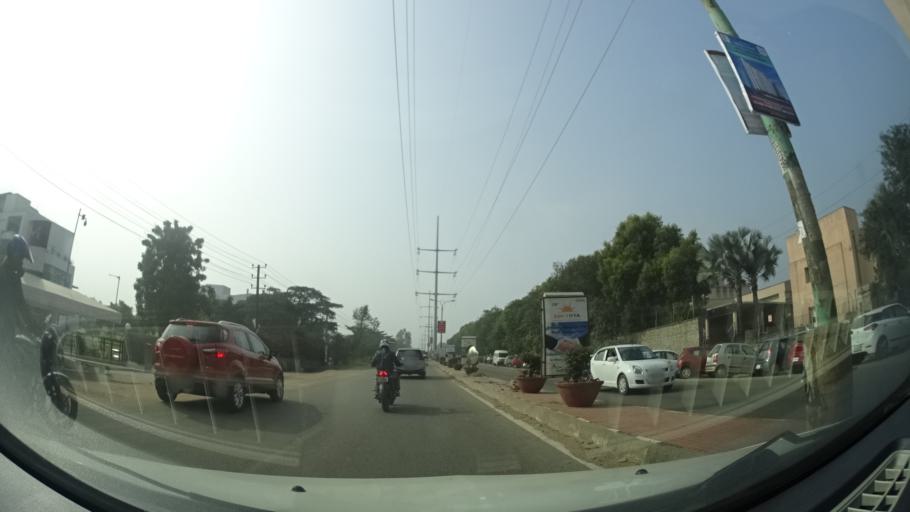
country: IN
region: Karnataka
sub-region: Bangalore Urban
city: Anekal
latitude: 12.8059
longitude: 77.6632
